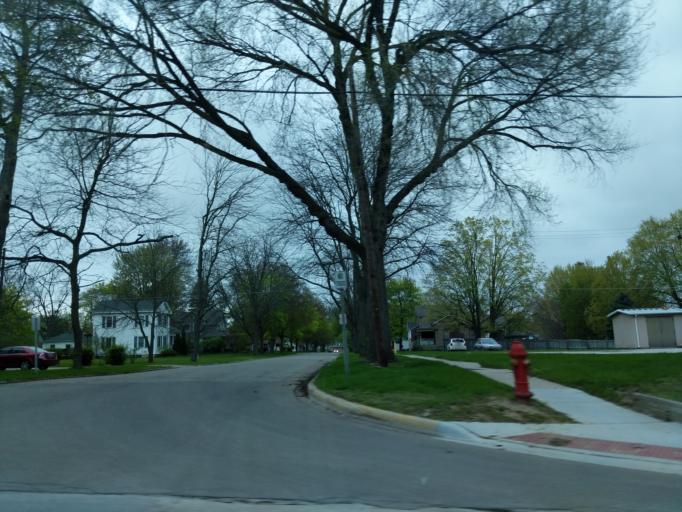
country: US
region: Michigan
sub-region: Tuscola County
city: Vassar
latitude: 43.3722
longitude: -83.5866
